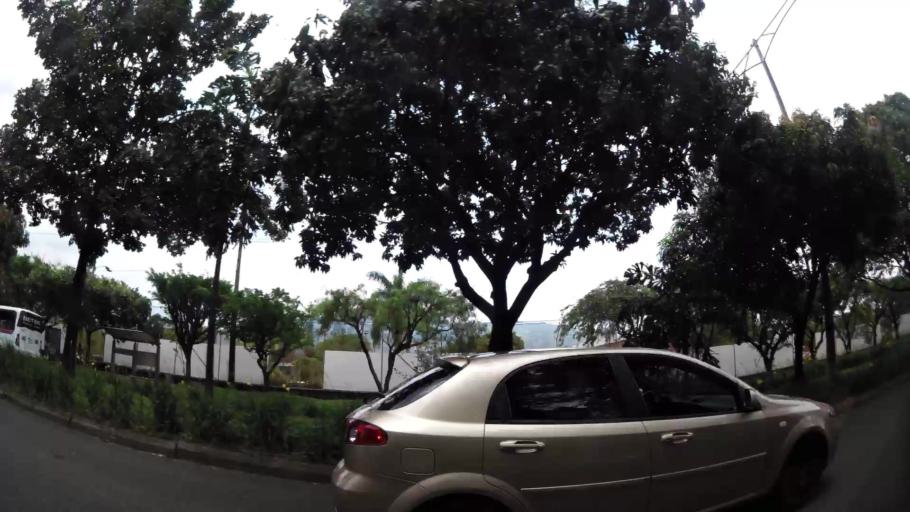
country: CO
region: Antioquia
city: Envigado
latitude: 6.1688
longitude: -75.5968
